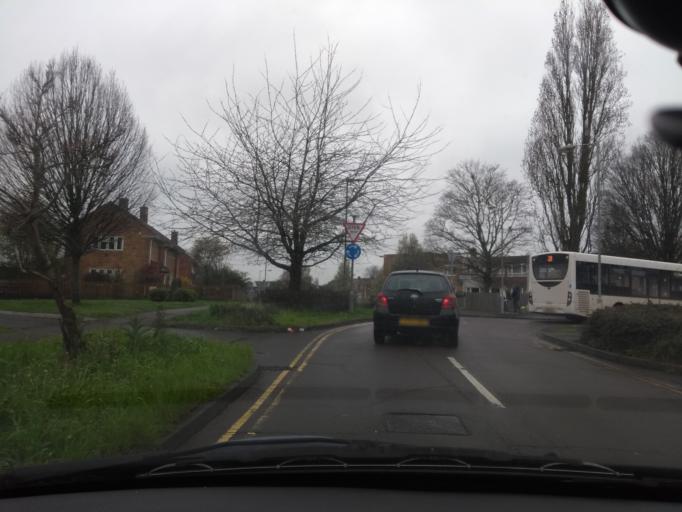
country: GB
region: England
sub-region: Somerset
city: Taunton
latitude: 51.0323
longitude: -3.0922
